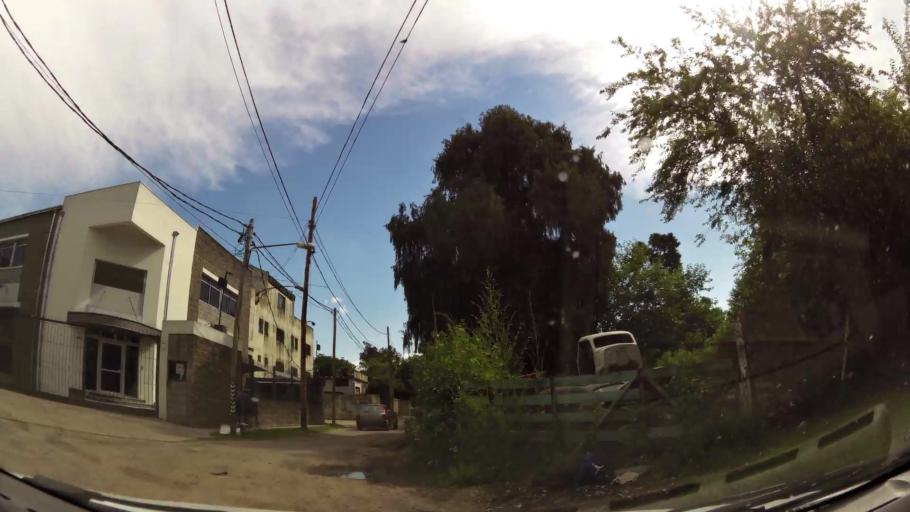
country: AR
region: Buenos Aires
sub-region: Partido de Merlo
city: Merlo
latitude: -34.6295
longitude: -58.7011
